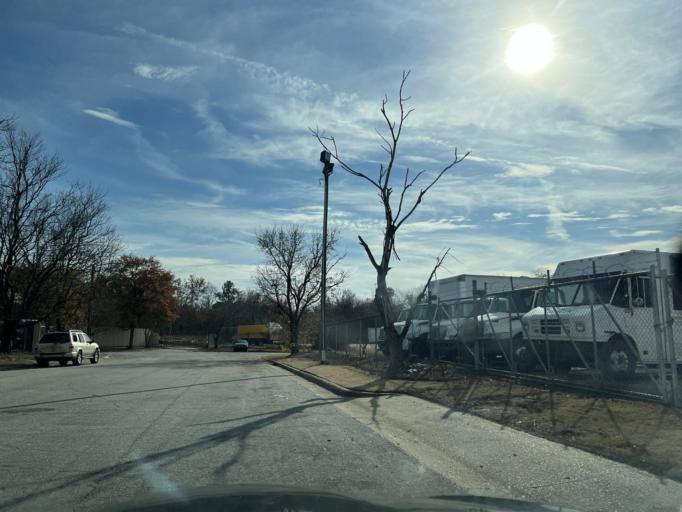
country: US
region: North Carolina
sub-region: Wake County
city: Raleigh
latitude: 35.7578
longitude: -78.6372
